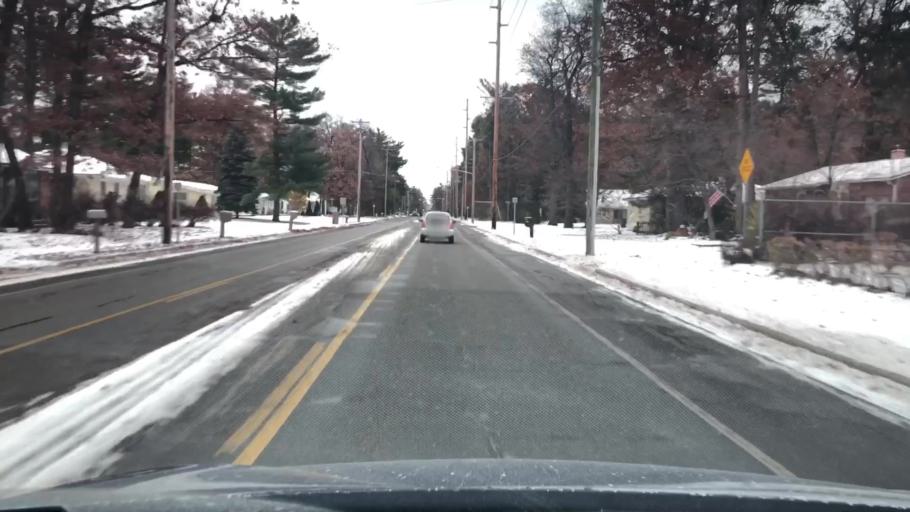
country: US
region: Michigan
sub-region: Grand Traverse County
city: Traverse City
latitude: 44.7586
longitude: -85.5854
